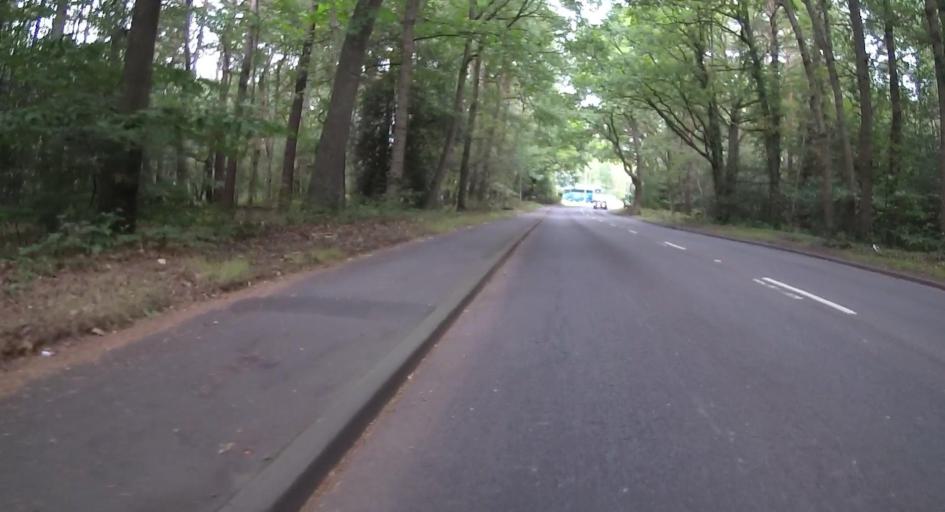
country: GB
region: England
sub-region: Surrey
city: Woking
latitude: 51.3317
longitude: -0.5450
